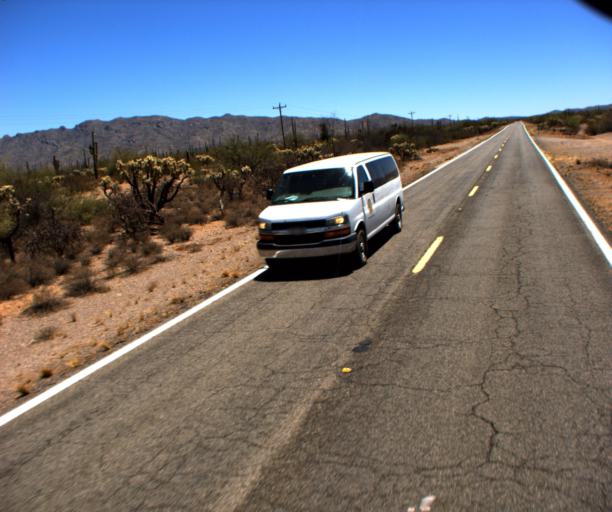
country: US
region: Arizona
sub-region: Pima County
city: Sells
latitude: 32.1827
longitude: -112.2954
